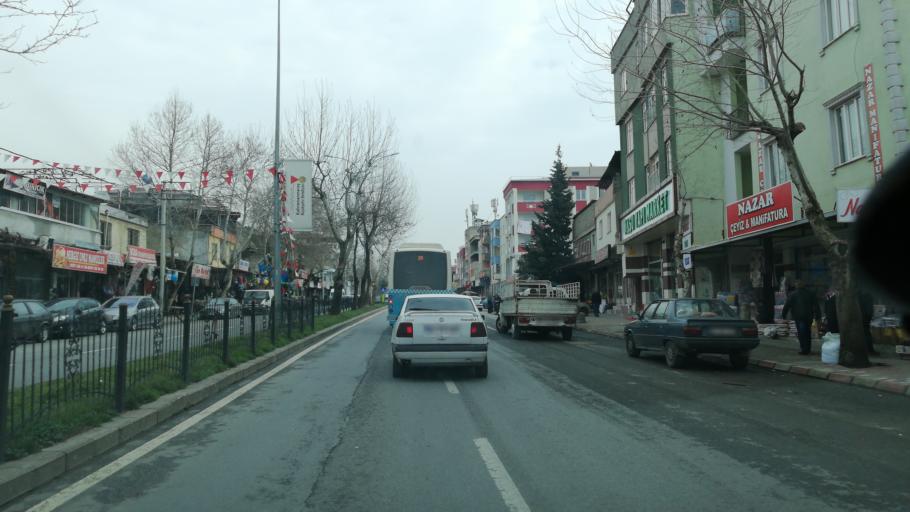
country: TR
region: Kahramanmaras
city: Kahramanmaras
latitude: 37.5736
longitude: 36.9022
